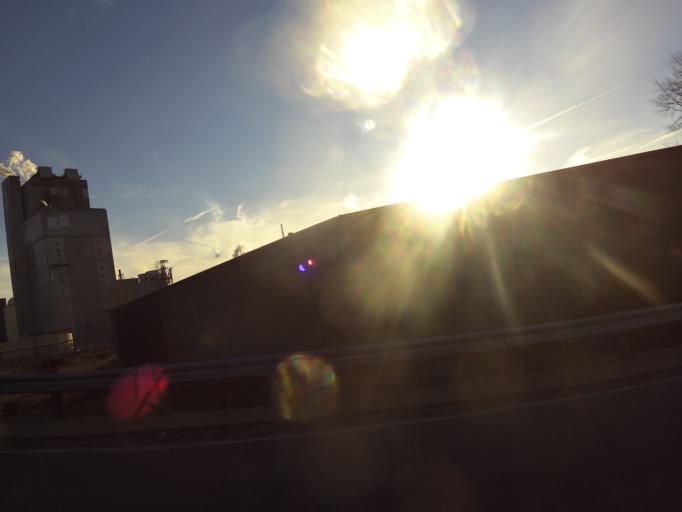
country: US
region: Virginia
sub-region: City of Franklin
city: Franklin
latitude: 36.6834
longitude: -76.9123
